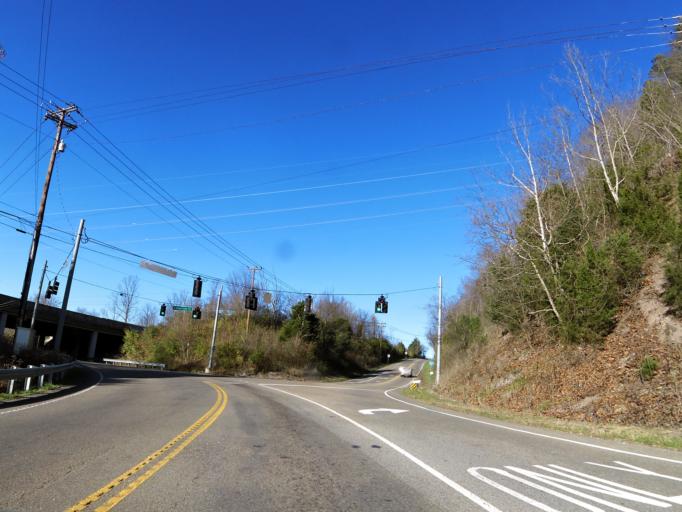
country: US
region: Tennessee
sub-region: Knox County
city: Knoxville
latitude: 36.0343
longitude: -83.9973
